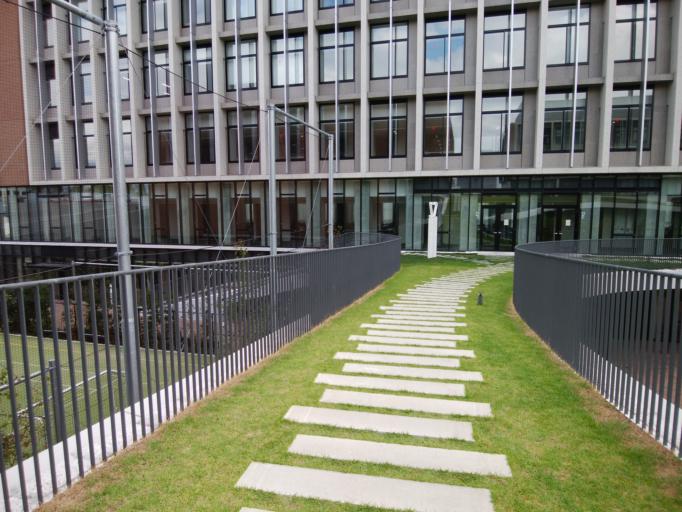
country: JP
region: Aichi
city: Nagoya-shi
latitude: 35.1893
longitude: 136.9447
